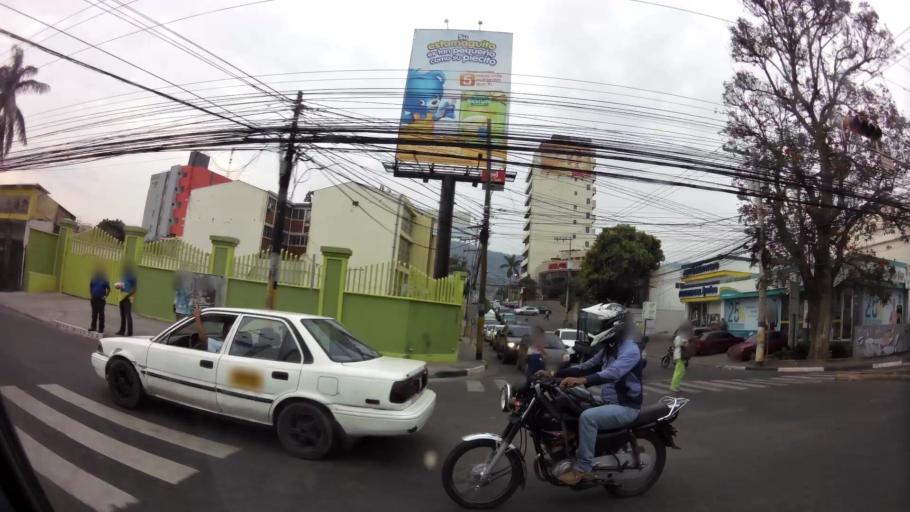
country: HN
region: Francisco Morazan
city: Tegucigalpa
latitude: 14.1000
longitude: -87.1913
